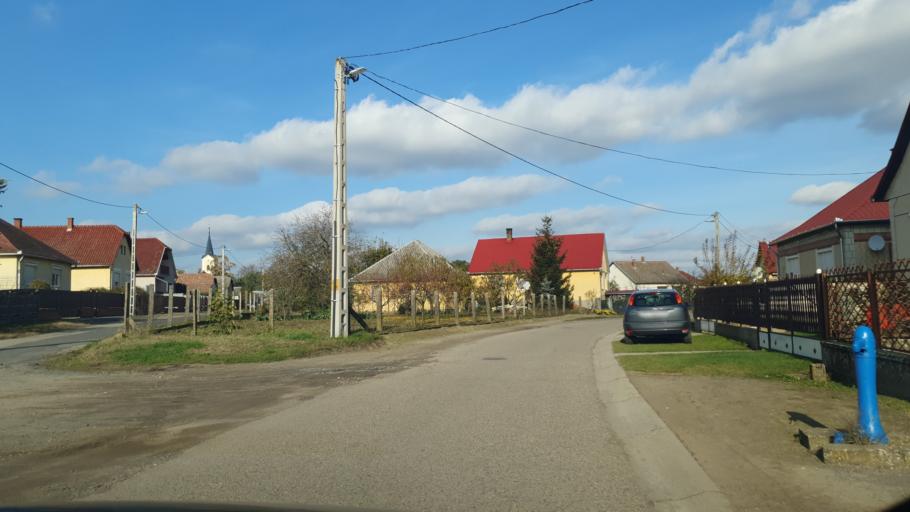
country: HU
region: Szabolcs-Szatmar-Bereg
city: Nyirtass
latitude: 48.1134
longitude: 22.0244
